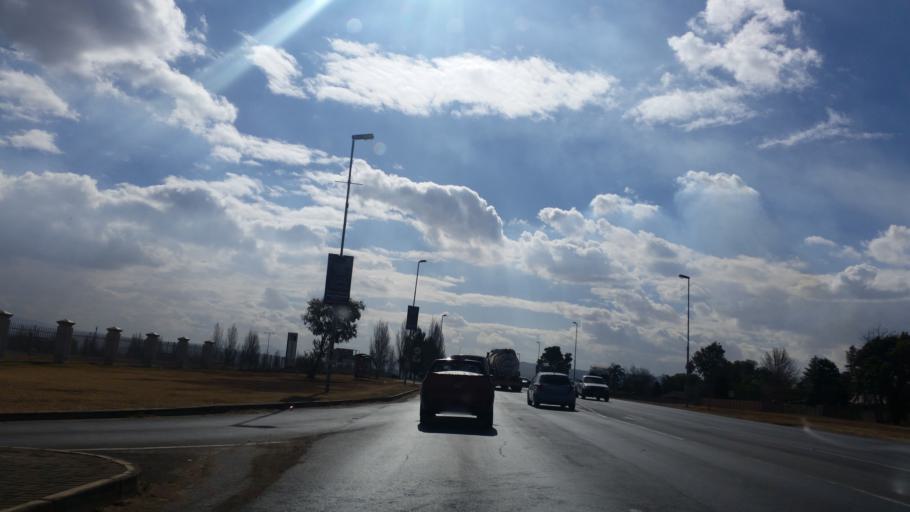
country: ZA
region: KwaZulu-Natal
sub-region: Amajuba District Municipality
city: Newcastle
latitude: -27.7801
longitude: 29.9473
